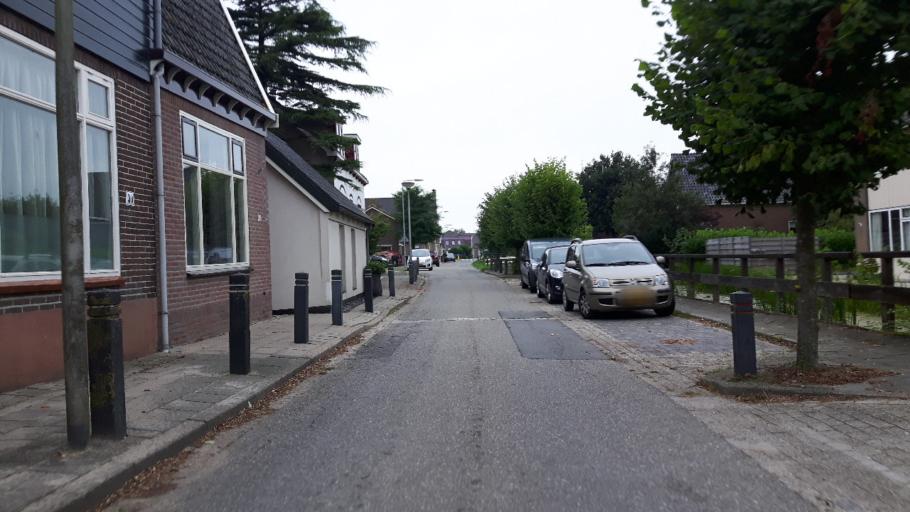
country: NL
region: South Holland
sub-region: Gemeente Nieuwkoop
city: Nieuwkoop
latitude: 52.1789
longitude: 4.7851
